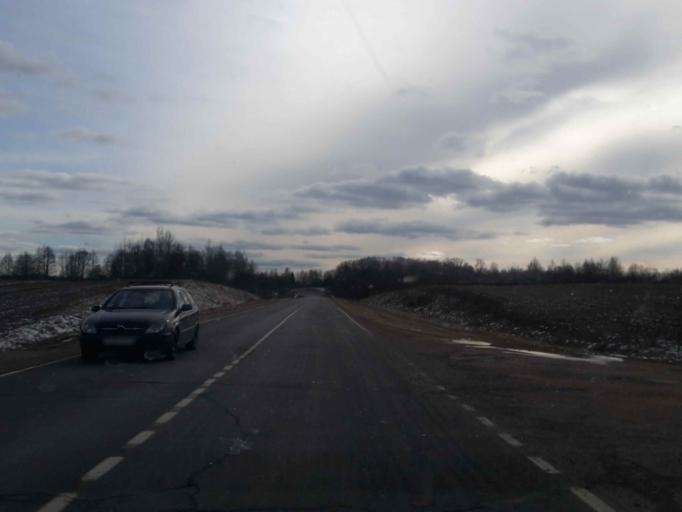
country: BY
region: Minsk
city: Myadzyel
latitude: 54.9737
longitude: 26.8981
